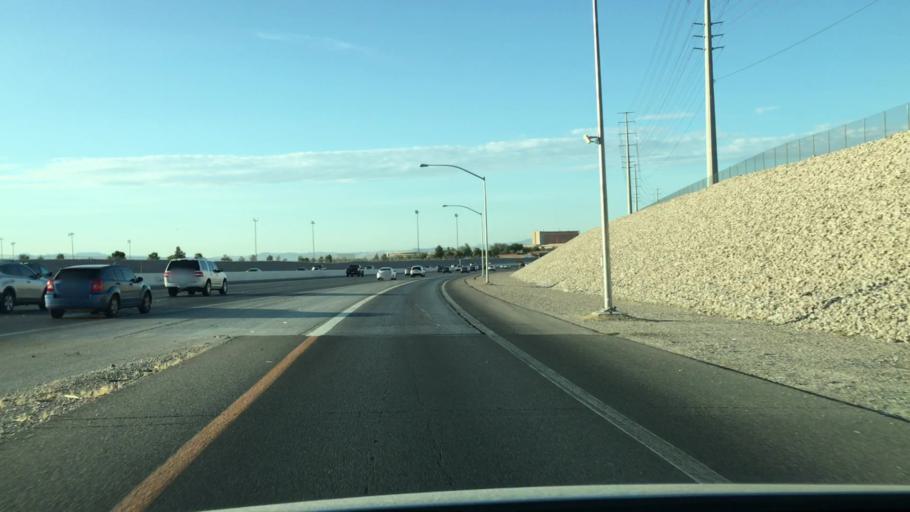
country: US
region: Nevada
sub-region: Clark County
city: Summerlin South
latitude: 36.1764
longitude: -115.3392
